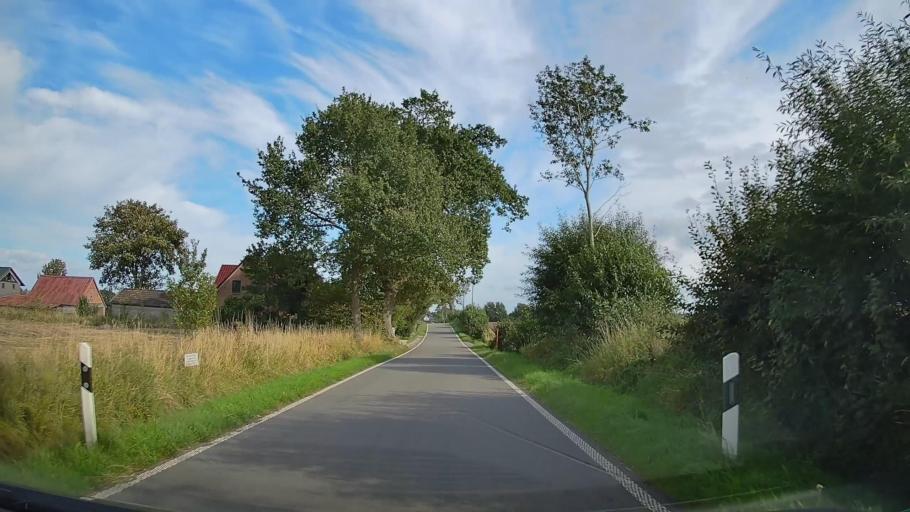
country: DE
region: Schleswig-Holstein
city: Steinbergkirche
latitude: 54.8010
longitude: 9.7469
